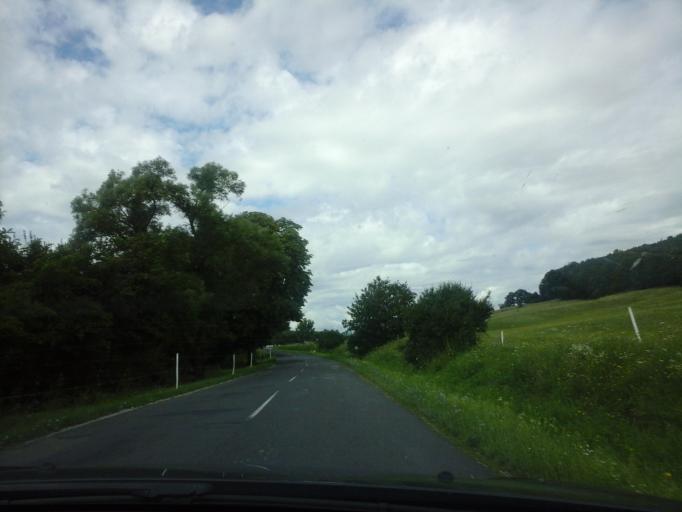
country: HU
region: Borsod-Abauj-Zemplen
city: Rudabanya
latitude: 48.3928
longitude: 20.5426
